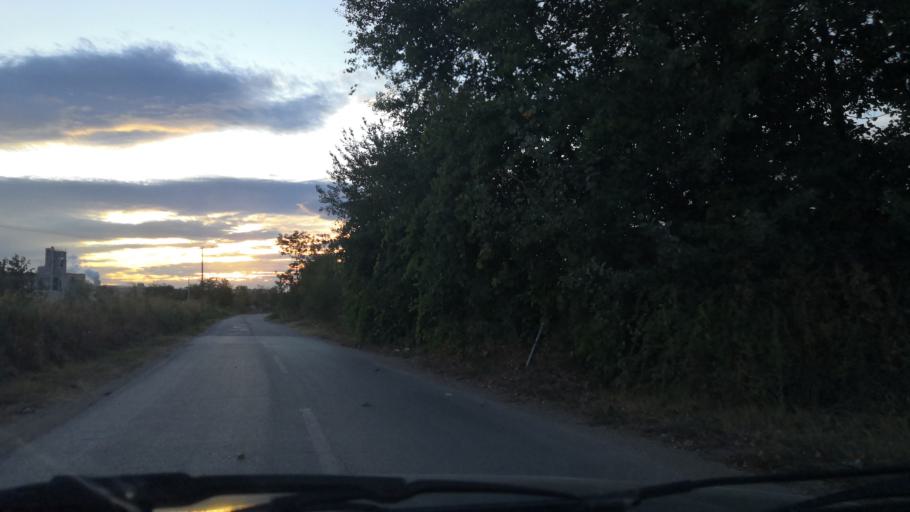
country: RO
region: Mehedinti
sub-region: Comuna Gruia
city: Izvoarele
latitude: 44.2884
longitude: 22.6169
